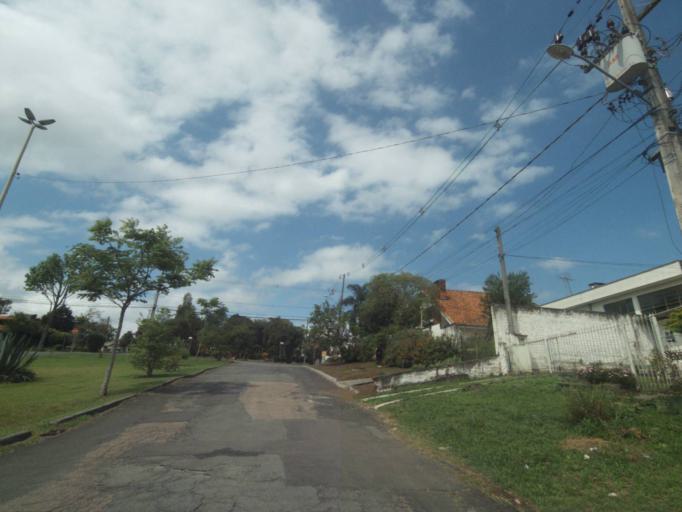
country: BR
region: Parana
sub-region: Pinhais
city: Pinhais
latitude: -25.4180
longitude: -49.2121
